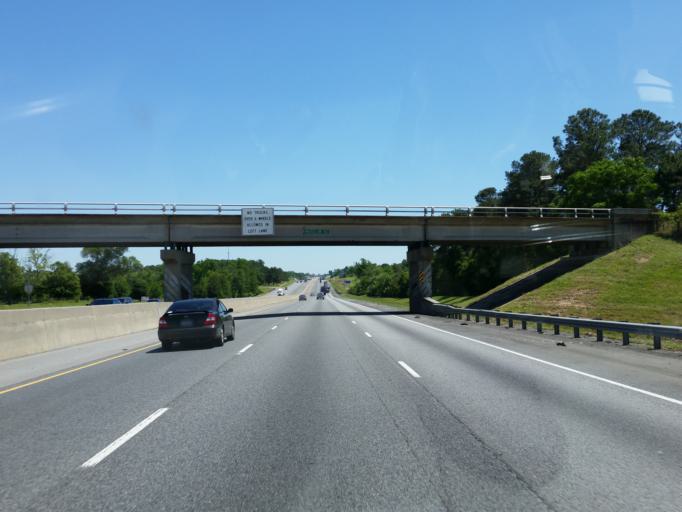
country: US
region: Georgia
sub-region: Turner County
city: Ashburn
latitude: 31.7563
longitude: -83.6675
